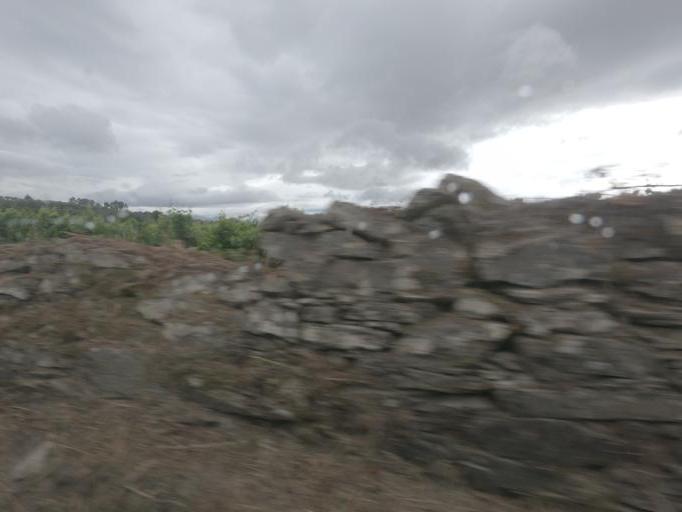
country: PT
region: Vila Real
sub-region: Sabrosa
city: Sabrosa
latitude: 41.2545
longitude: -7.5027
